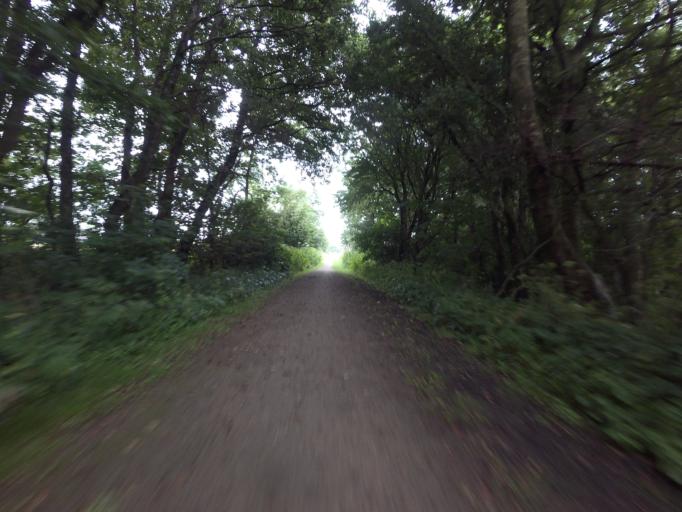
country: DK
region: North Denmark
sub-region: Alborg Kommune
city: Vadum
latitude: 57.1146
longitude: 9.8773
